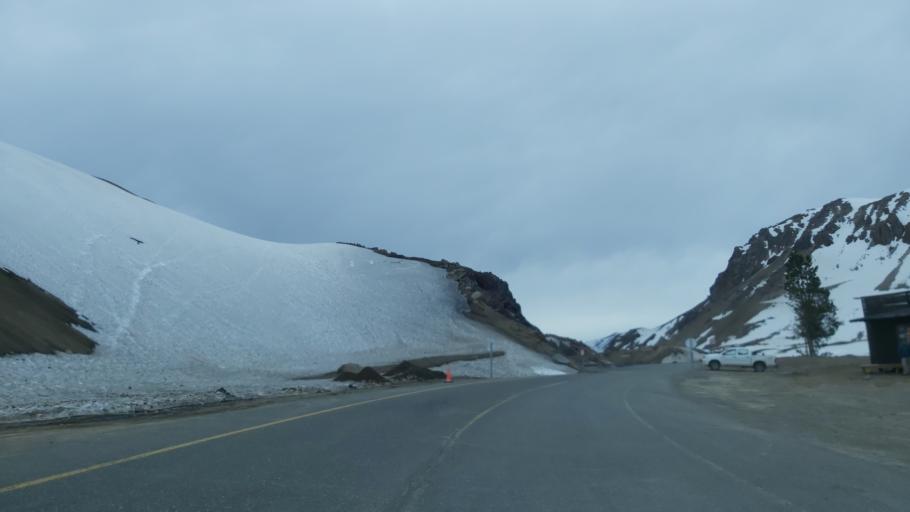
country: CL
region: Maule
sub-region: Provincia de Linares
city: Colbun
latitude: -36.0074
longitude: -70.5593
